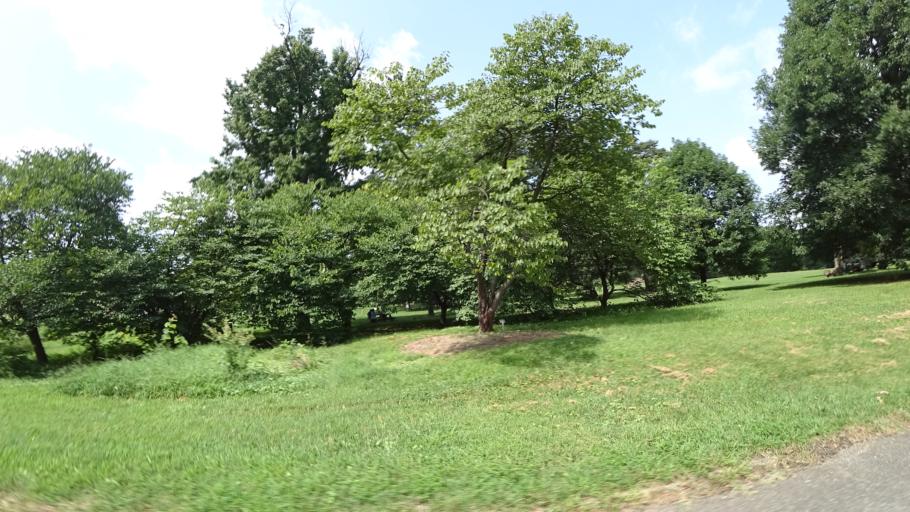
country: US
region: Maryland
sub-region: Prince George's County
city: Colmar Manor
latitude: 38.9072
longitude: -76.9684
